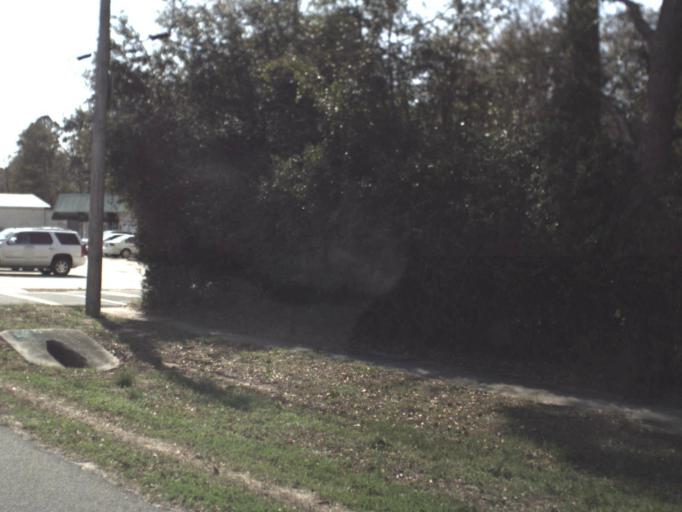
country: US
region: Florida
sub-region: Bay County
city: Lynn Haven
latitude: 30.2349
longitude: -85.6557
